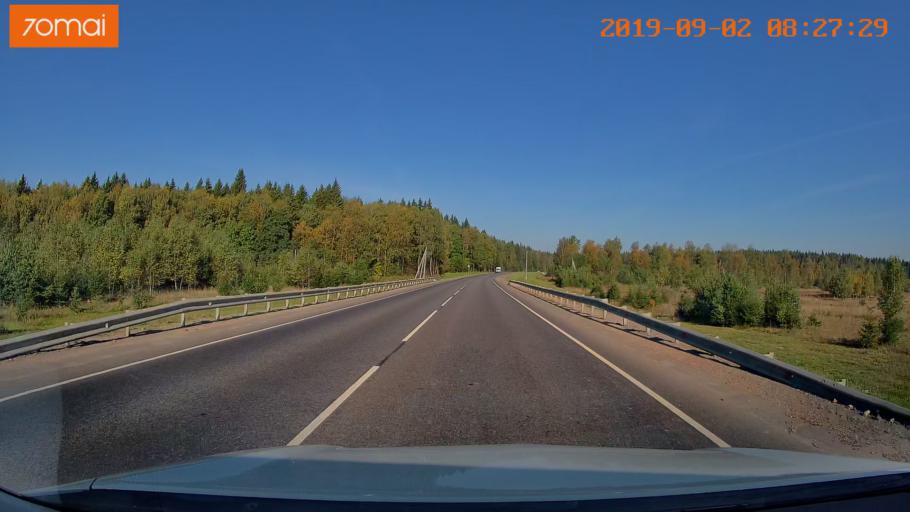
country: RU
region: Kaluga
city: Maloyaroslavets
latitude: 54.9822
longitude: 36.4153
